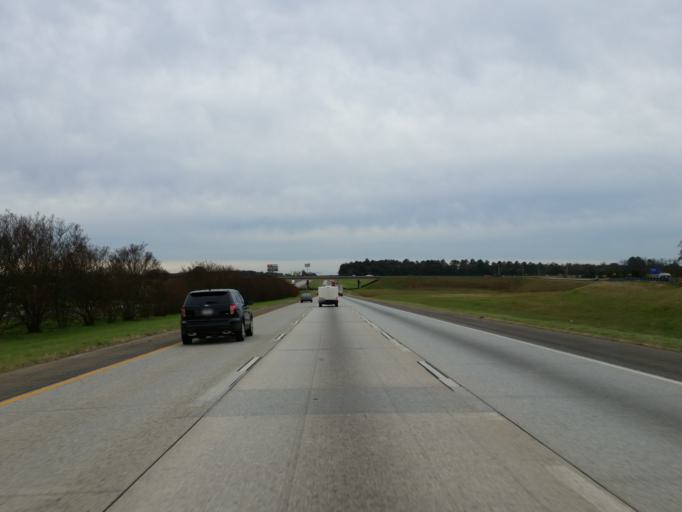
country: US
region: Georgia
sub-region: Peach County
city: Byron
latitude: 32.5914
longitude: -83.7432
